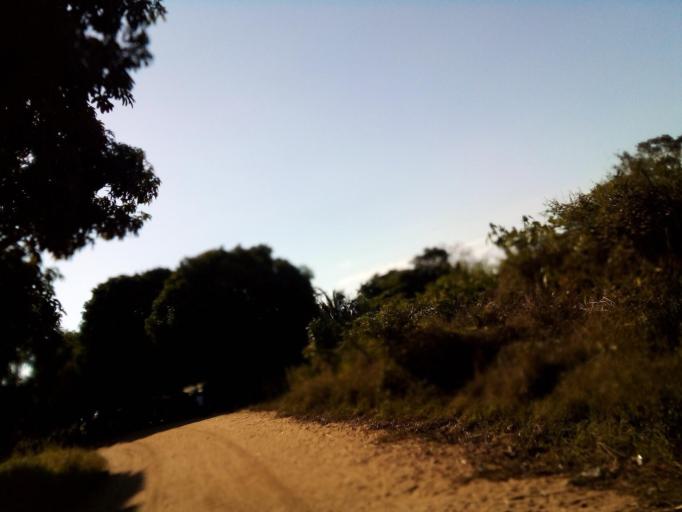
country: MZ
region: Zambezia
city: Quelimane
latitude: -17.4871
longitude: 36.5594
